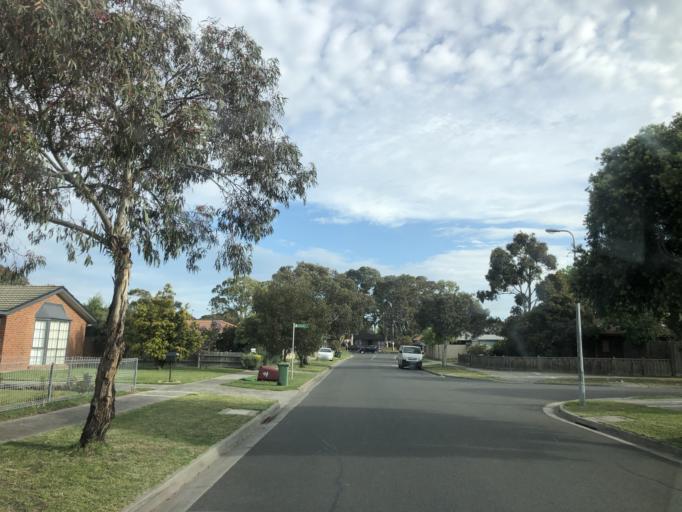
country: AU
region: Victoria
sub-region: Casey
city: Hampton Park
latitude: -38.0257
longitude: 145.2569
